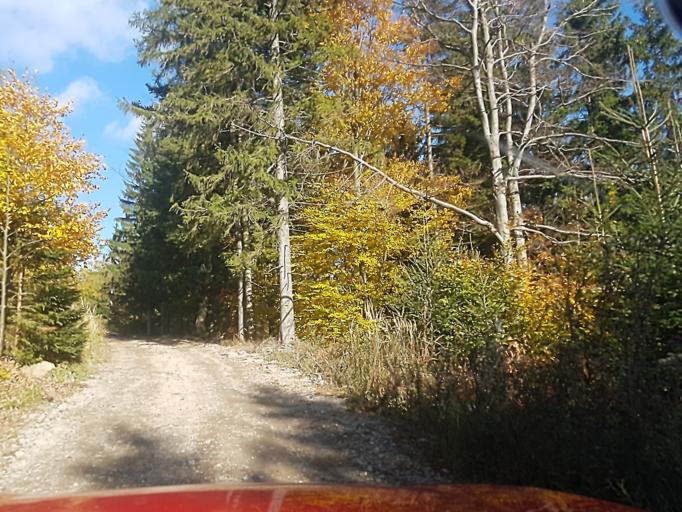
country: SK
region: Zilinsky
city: Ruzomberok
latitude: 49.1334
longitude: 19.3599
